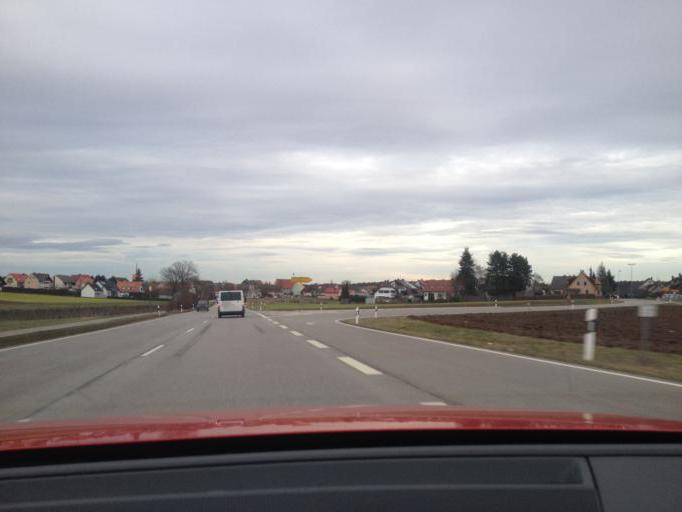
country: DE
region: Bavaria
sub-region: Regierungsbezirk Mittelfranken
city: Rosstal
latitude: 49.3801
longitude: 10.9261
